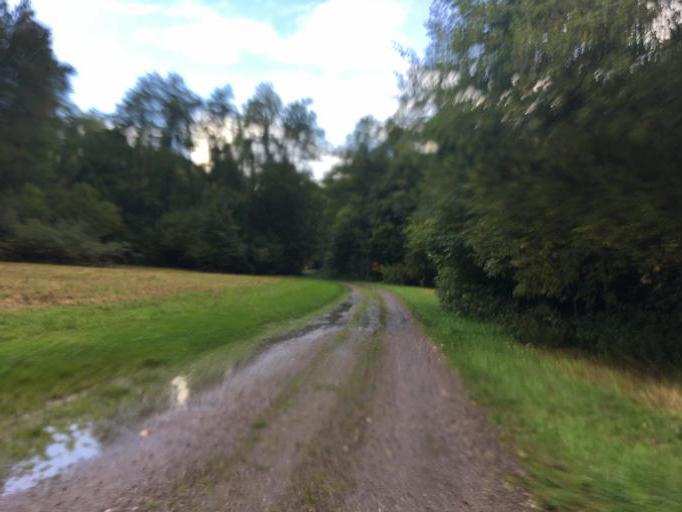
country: SE
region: Soedermanland
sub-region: Eskilstuna Kommun
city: Eskilstuna
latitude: 59.4582
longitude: 16.6572
